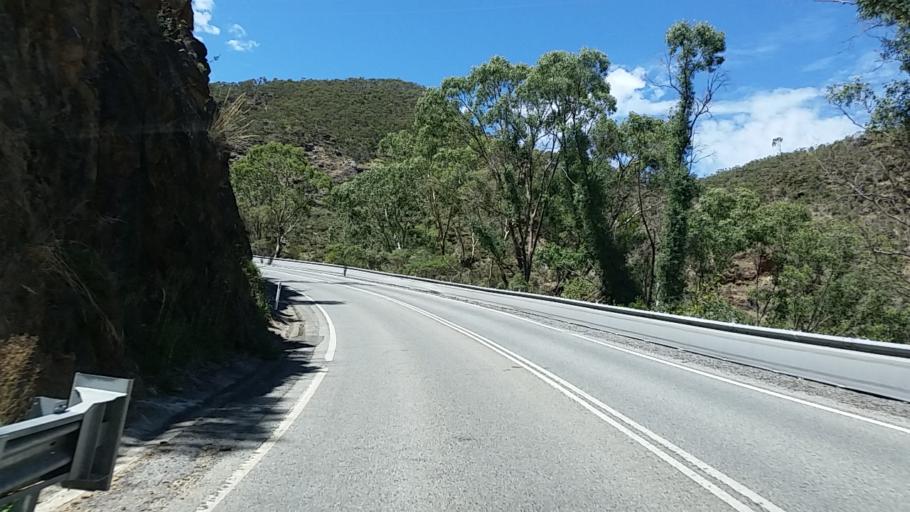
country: AU
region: South Australia
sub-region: Campbelltown
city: Athelstone
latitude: -34.8640
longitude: 138.7624
